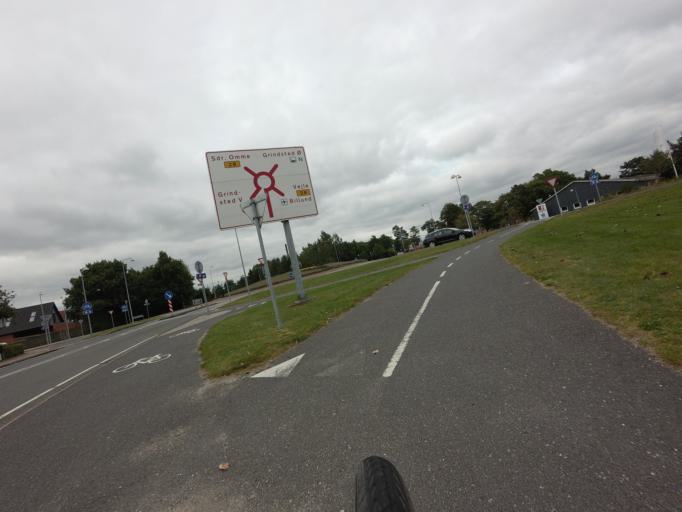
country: DK
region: South Denmark
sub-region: Billund Kommune
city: Grindsted
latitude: 55.7609
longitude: 8.9299
